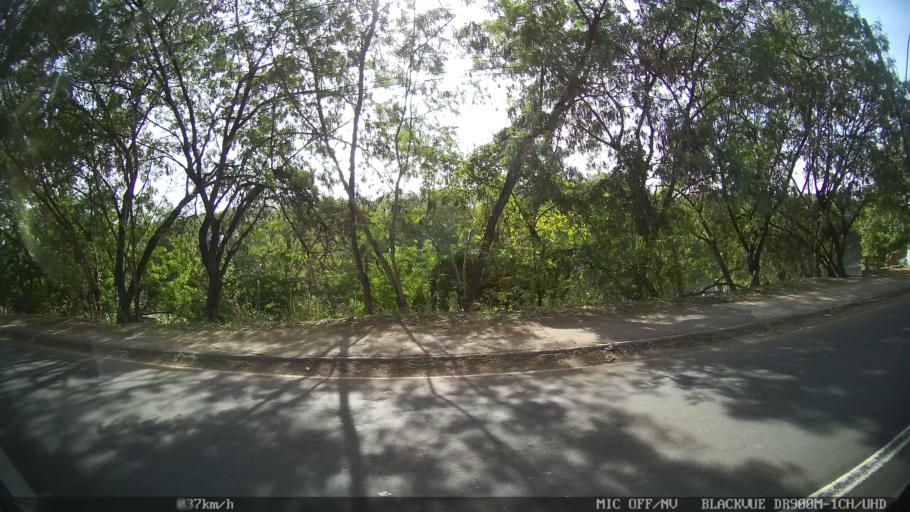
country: BR
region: Sao Paulo
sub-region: Piracicaba
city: Piracicaba
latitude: -22.7246
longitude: -47.6699
